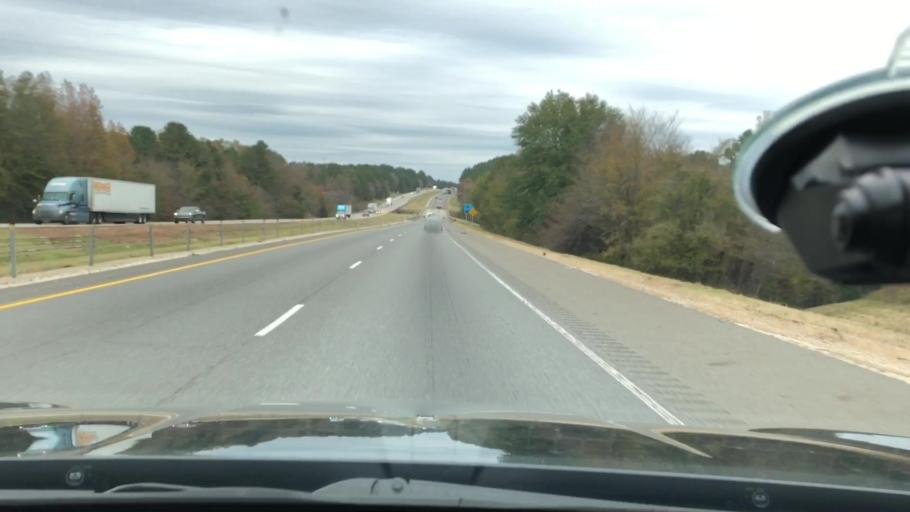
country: US
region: Arkansas
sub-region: Hot Spring County
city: Malvern
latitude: 34.3141
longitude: -92.9365
